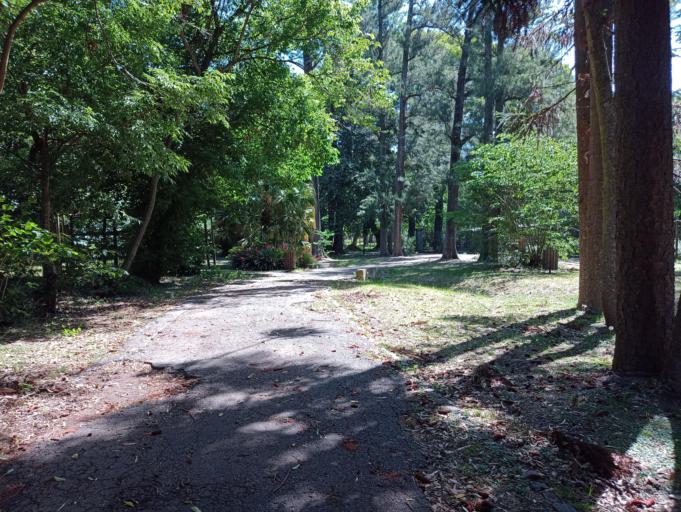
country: AR
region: Buenos Aires
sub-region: Partido de La Plata
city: La Plata
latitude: -34.9070
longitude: -57.9352
